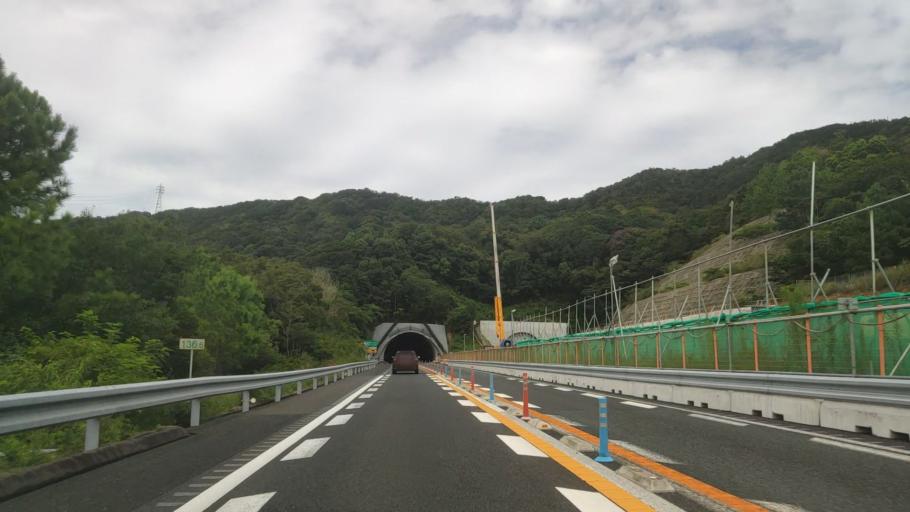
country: JP
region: Wakayama
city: Gobo
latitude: 33.8480
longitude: 135.2171
